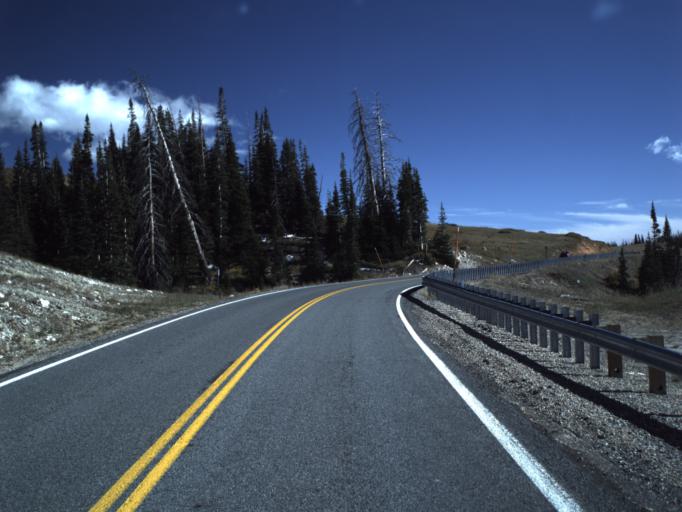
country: US
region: Utah
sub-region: Iron County
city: Parowan
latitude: 37.6759
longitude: -112.8422
